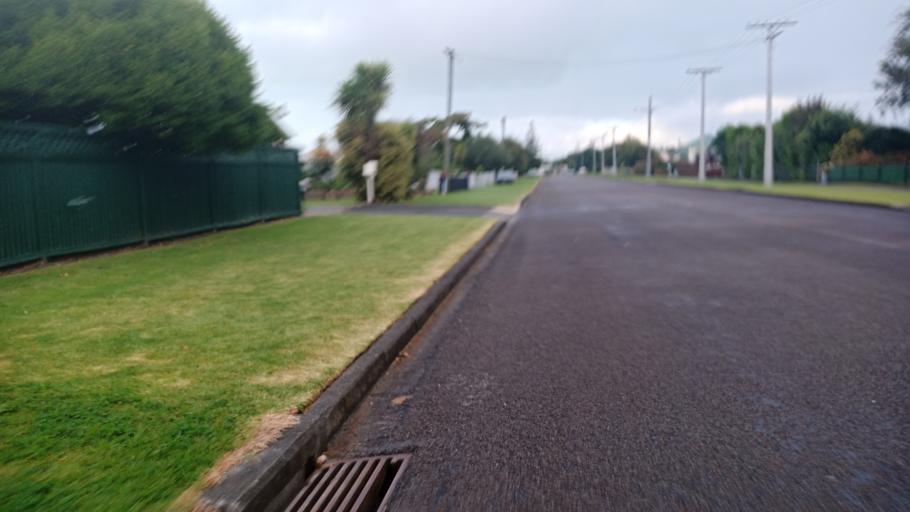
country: NZ
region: Gisborne
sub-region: Gisborne District
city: Gisborne
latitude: -38.6411
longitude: 178.0130
